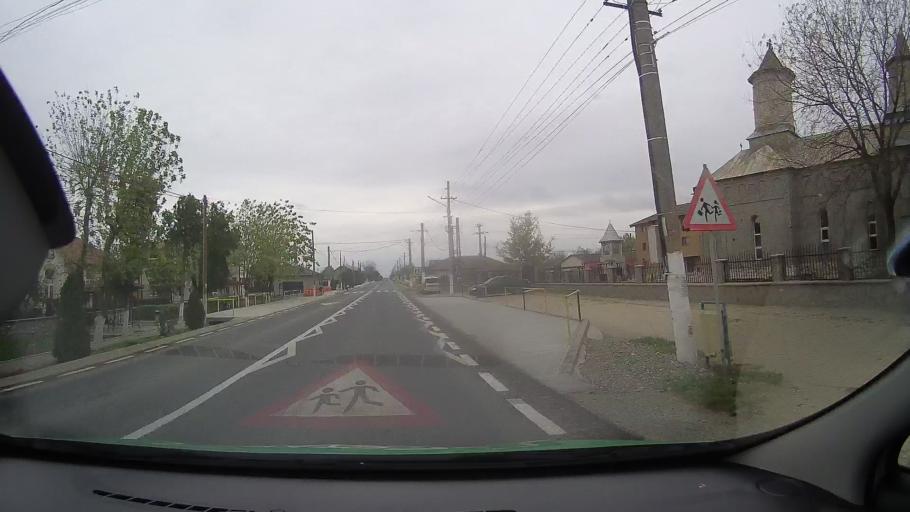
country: RO
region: Constanta
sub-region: Comuna Nicolae Balcescu
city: Nicolae Balcescu
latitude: 44.3881
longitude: 28.3803
